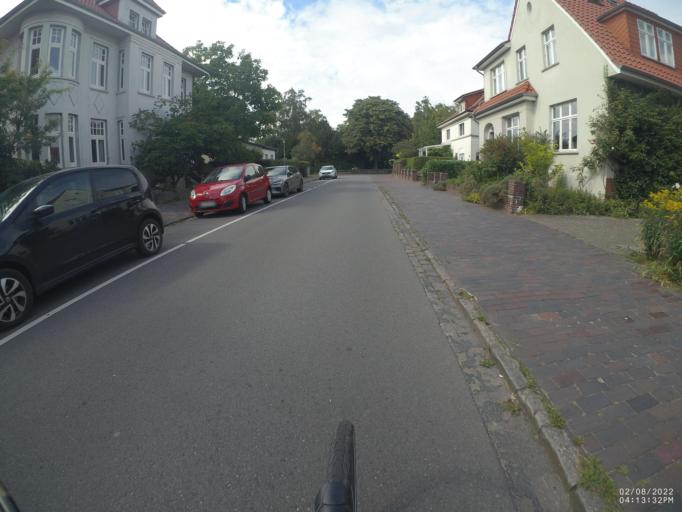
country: DE
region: Lower Saxony
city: Oldenburg
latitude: 53.1521
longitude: 8.2075
